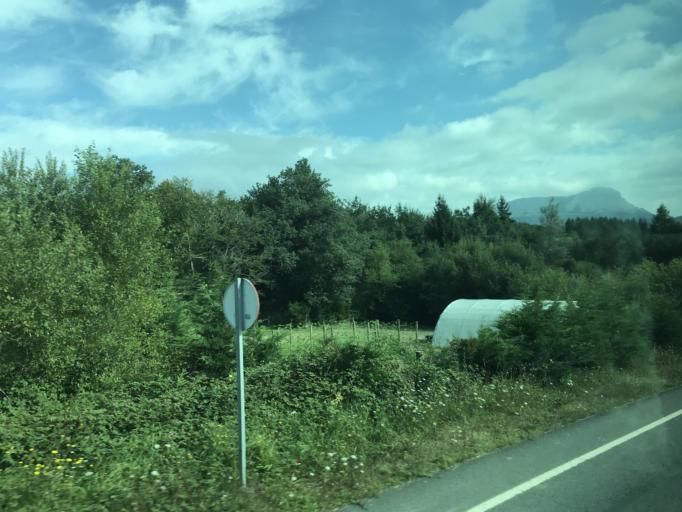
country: ES
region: Basque Country
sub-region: Bizkaia
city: Otxandio
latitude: 43.0356
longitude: -2.6501
